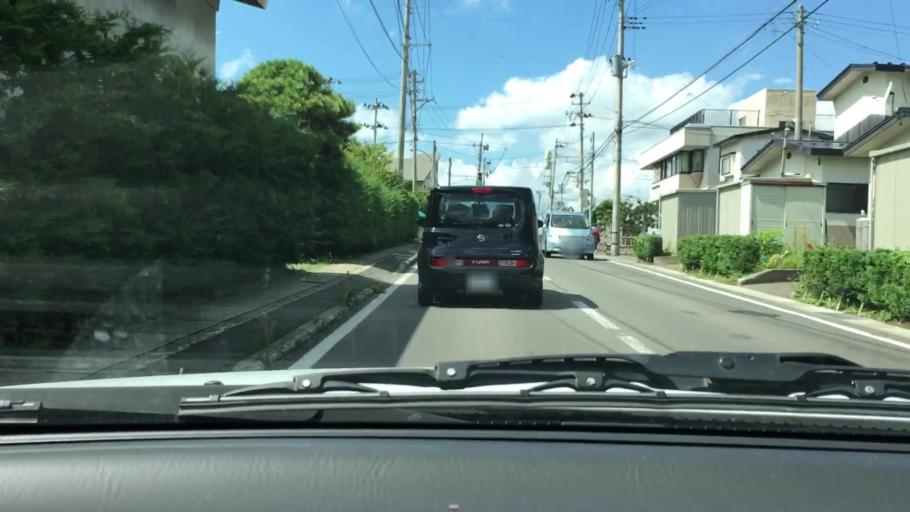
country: JP
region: Aomori
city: Hirosaki
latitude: 40.5865
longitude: 140.4631
